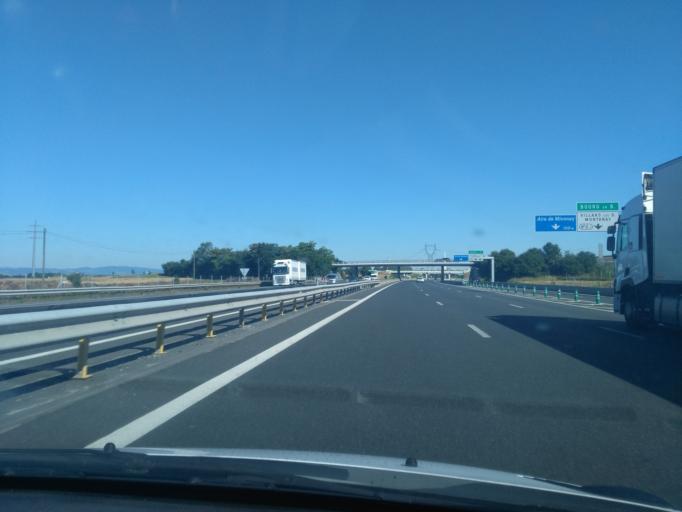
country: FR
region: Rhone-Alpes
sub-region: Departement de l'Ain
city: Mionnay
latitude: 45.8803
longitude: 4.8990
